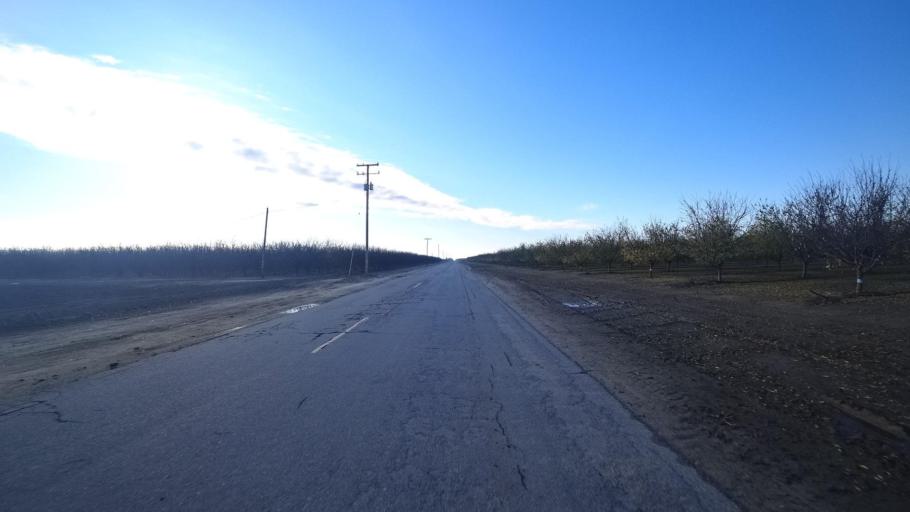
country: US
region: California
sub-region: Kern County
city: Delano
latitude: 35.7431
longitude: -119.3300
